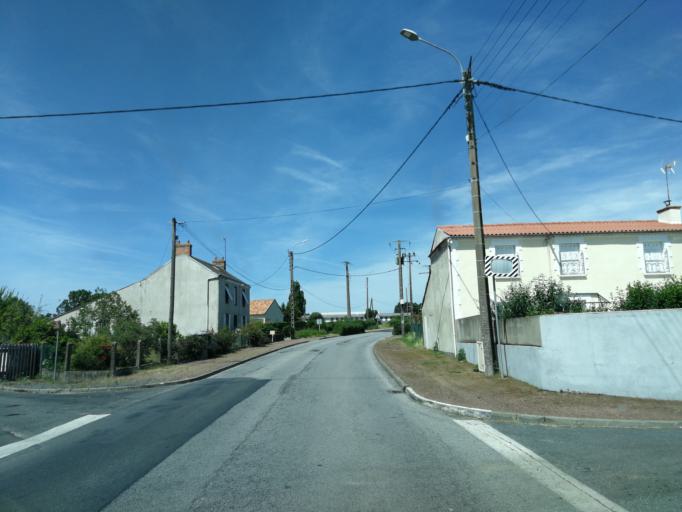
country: FR
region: Poitou-Charentes
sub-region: Departement des Deux-Sevres
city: Saint-Varent
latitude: 46.9022
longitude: -0.2877
